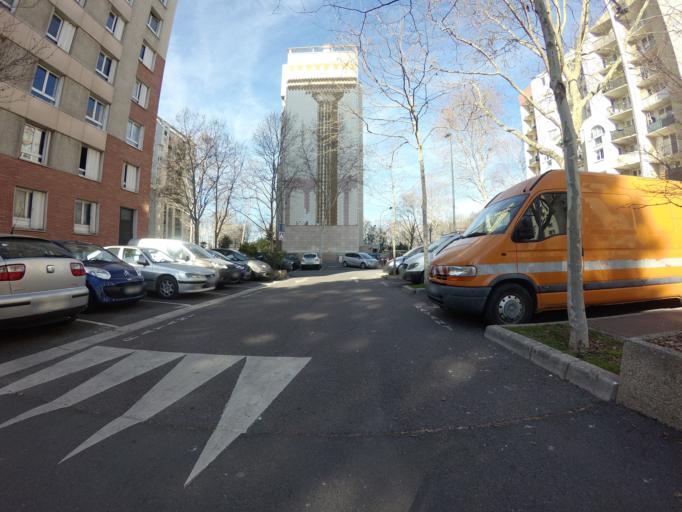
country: FR
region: Ile-de-France
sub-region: Departement des Hauts-de-Seine
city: Clichy
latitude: 48.9087
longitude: 2.3032
